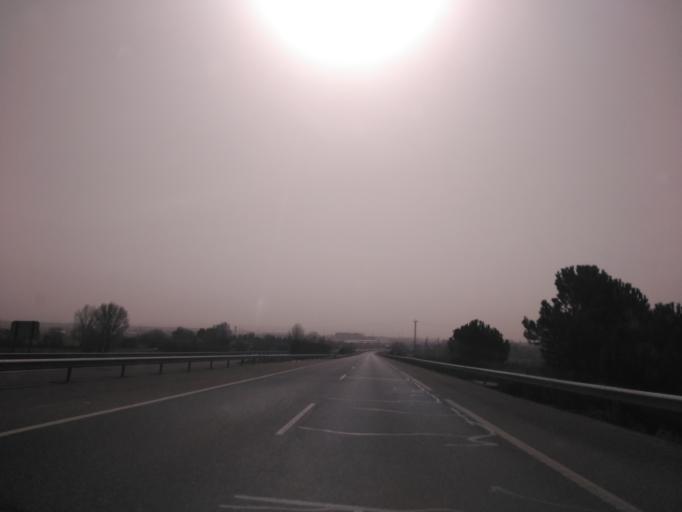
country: ES
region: Castille and Leon
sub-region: Provincia de Palencia
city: Villamuriel de Cerrato
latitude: 41.9799
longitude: -4.5013
